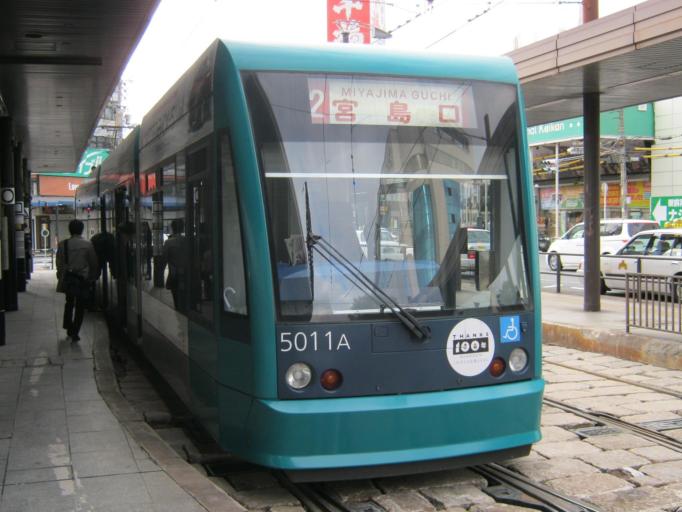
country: JP
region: Hiroshima
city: Hiroshima-shi
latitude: 34.3963
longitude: 132.4752
